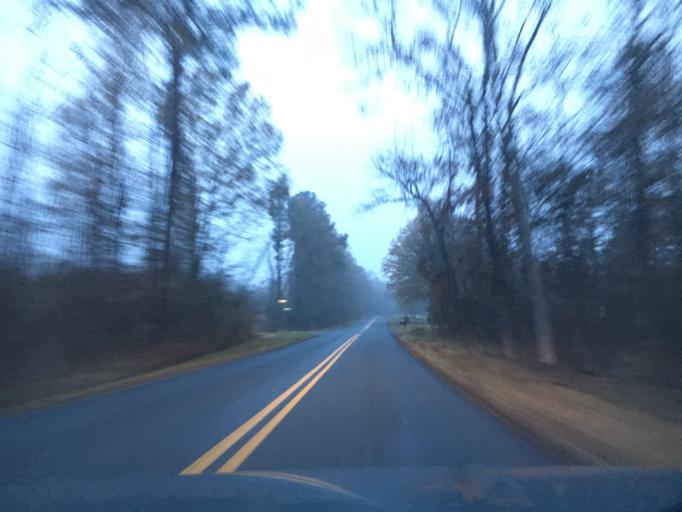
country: US
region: Virginia
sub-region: Halifax County
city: Mountain Road
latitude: 36.6804
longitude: -79.0213
